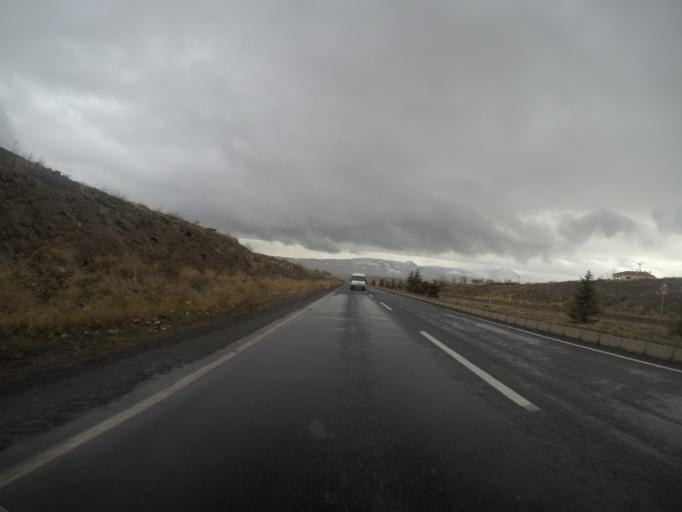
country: TR
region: Kayseri
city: Incesu
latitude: 38.6832
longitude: 35.1967
